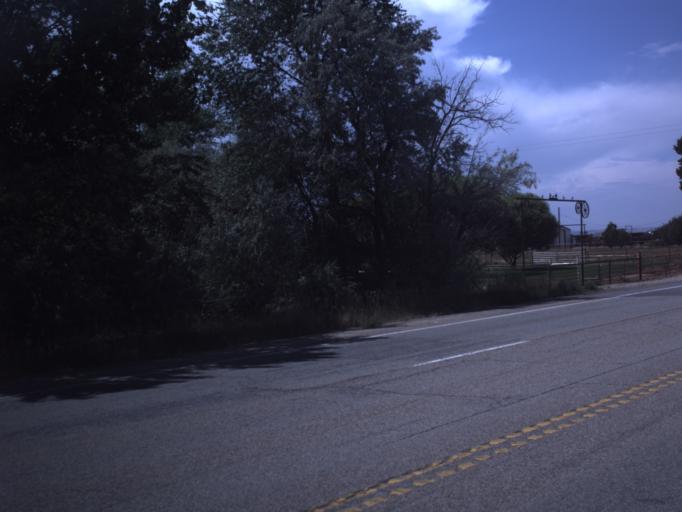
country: US
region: Utah
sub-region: Duchesne County
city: Roosevelt
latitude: 40.3019
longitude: -109.8992
